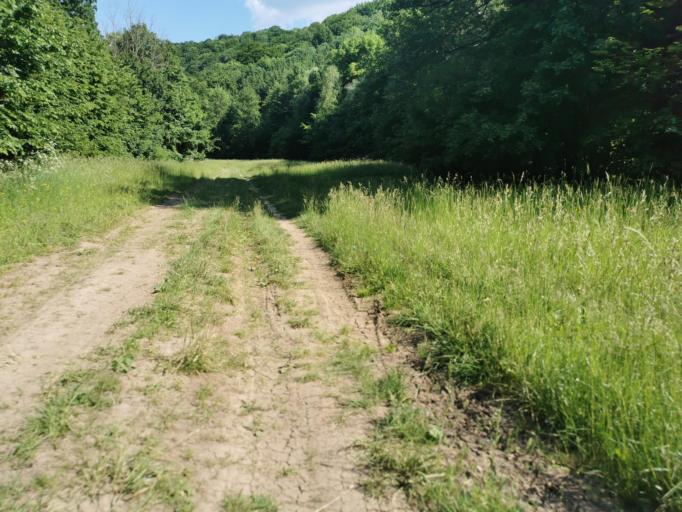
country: CZ
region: South Moravian
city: Straznice
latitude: 48.8432
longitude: 17.3317
